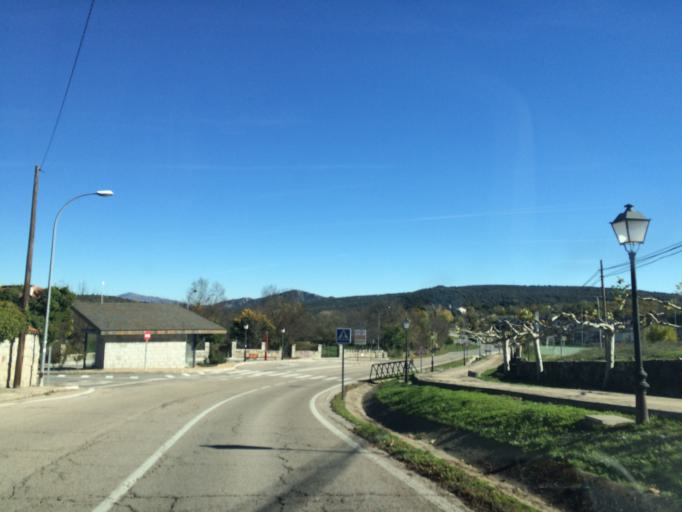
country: ES
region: Madrid
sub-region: Provincia de Madrid
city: Boalo
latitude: 40.7168
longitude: -3.9175
